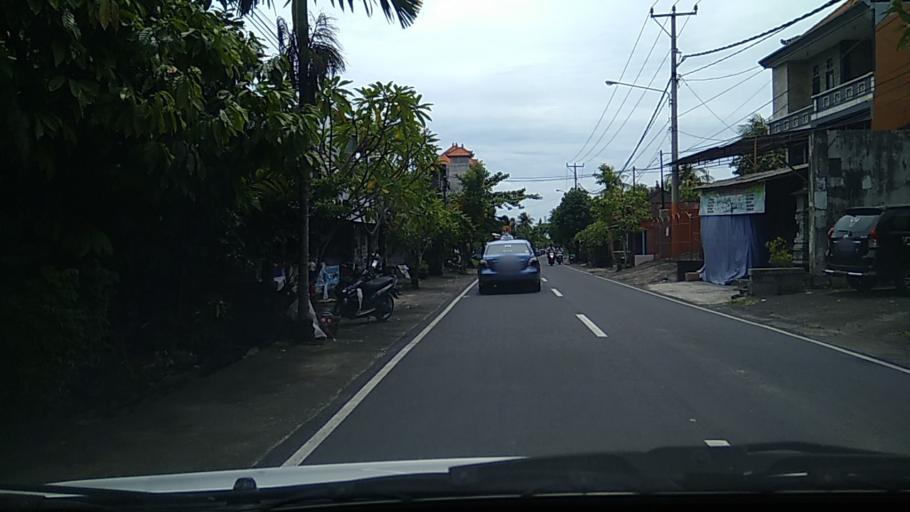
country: ID
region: Bali
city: Banjar Batanbuah
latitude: -8.6057
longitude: 115.1033
